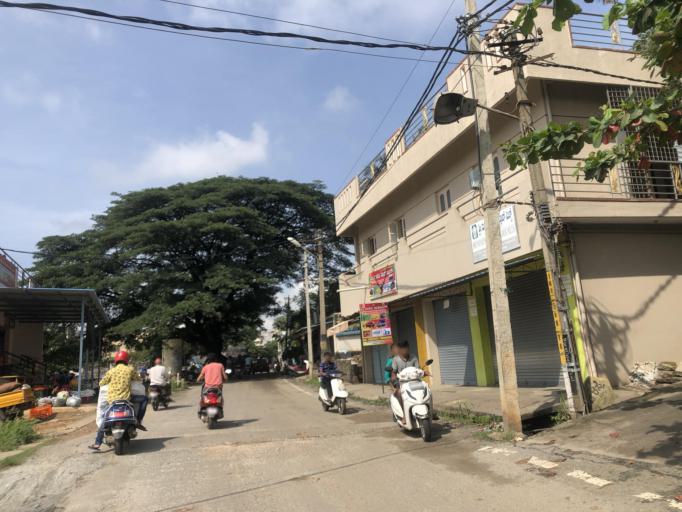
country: IN
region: Karnataka
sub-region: Bangalore Urban
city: Bangalore
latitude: 12.9246
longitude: 77.5309
